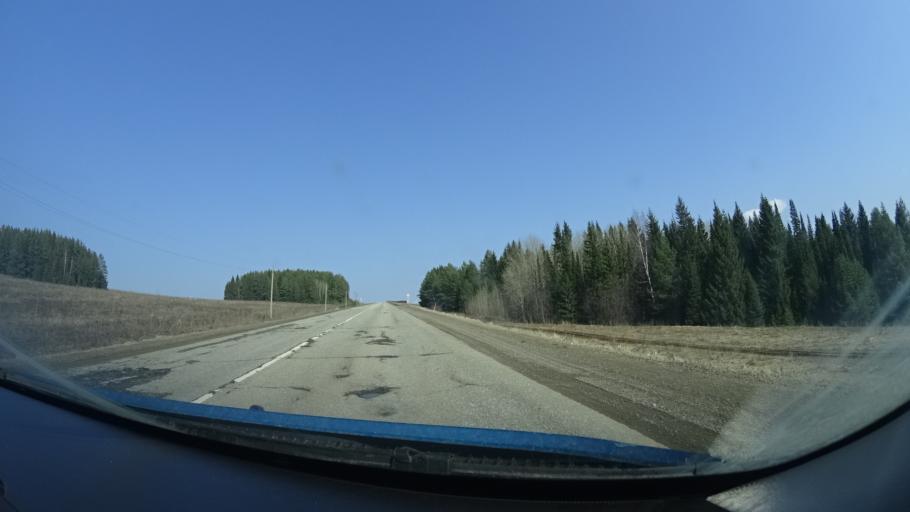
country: RU
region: Perm
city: Osa
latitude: 57.3112
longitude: 55.6205
